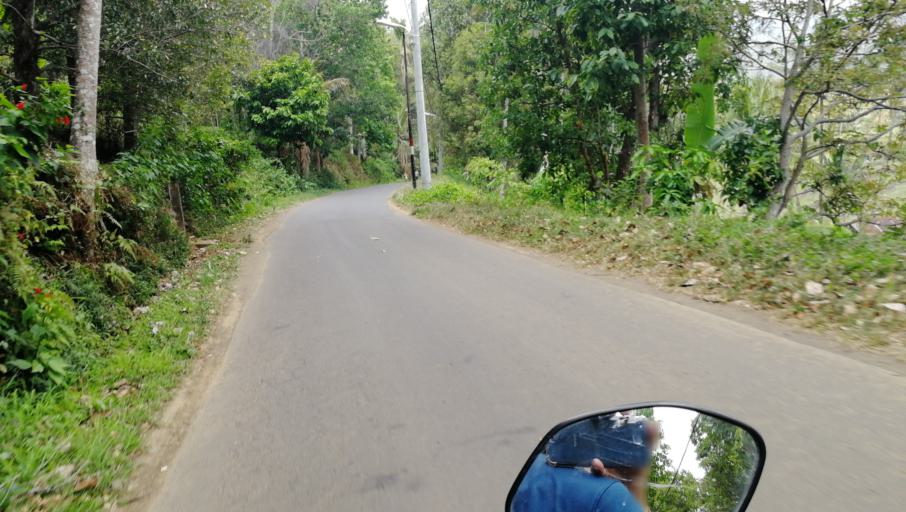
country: ID
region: Bali
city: Banjar Pedawa
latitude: -8.2656
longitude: 115.0443
